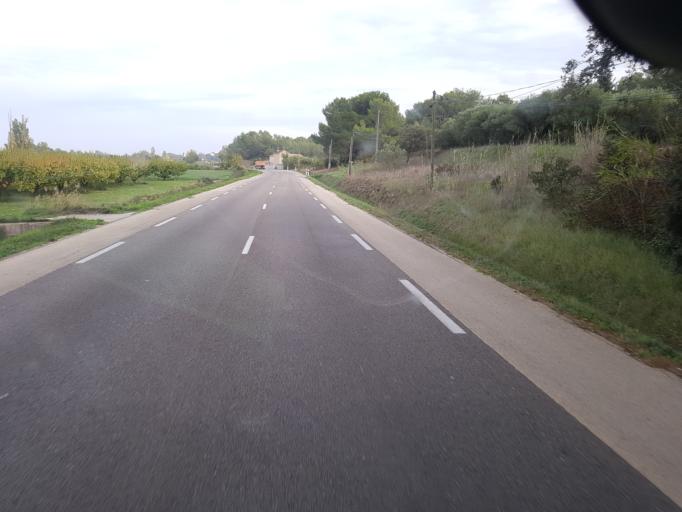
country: FR
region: Provence-Alpes-Cote d'Azur
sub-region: Departement des Bouches-du-Rhone
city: Barbentane
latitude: 43.8994
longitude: 4.7272
